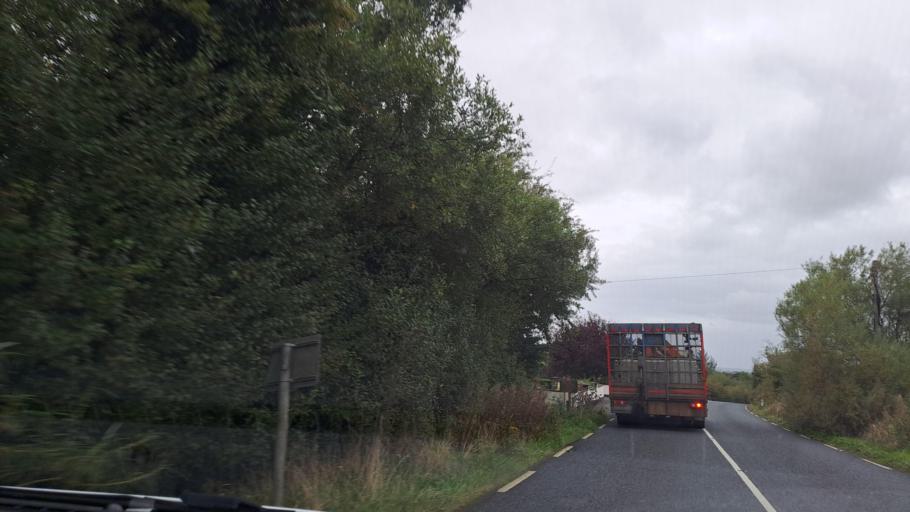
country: IE
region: Ulster
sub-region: County Monaghan
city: Castleblayney
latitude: 54.0921
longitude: -6.8393
